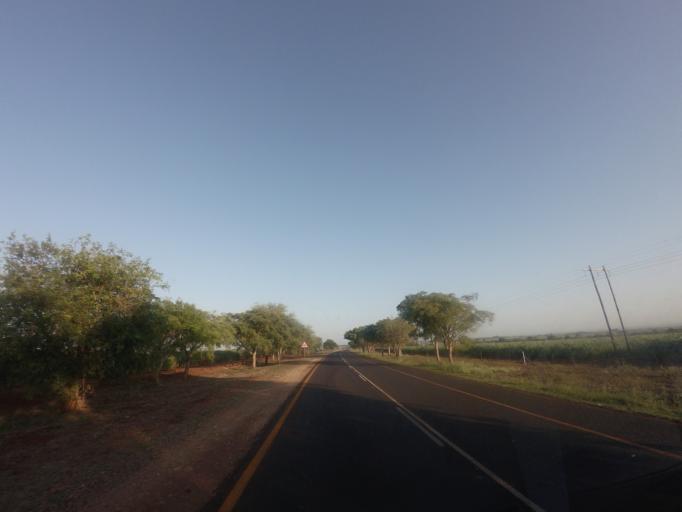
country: ZA
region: Mpumalanga
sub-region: Ehlanzeni District
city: Komatipoort
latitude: -25.3952
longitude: 31.9167
